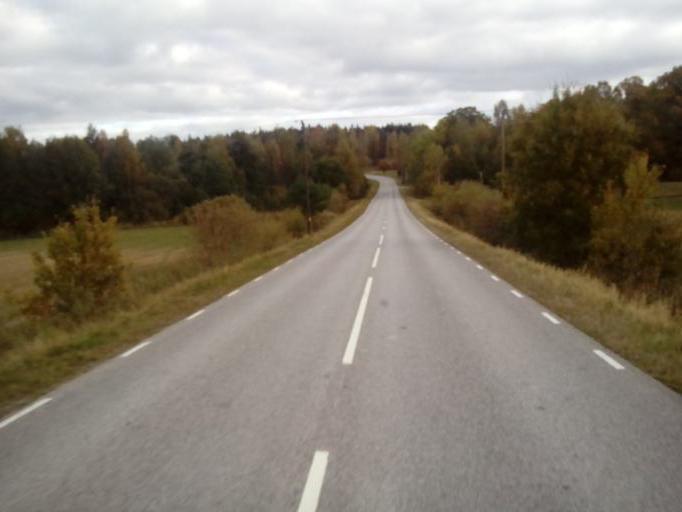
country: SE
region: Kalmar
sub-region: Vasterviks Kommun
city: Gamleby
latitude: 57.8792
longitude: 16.3169
